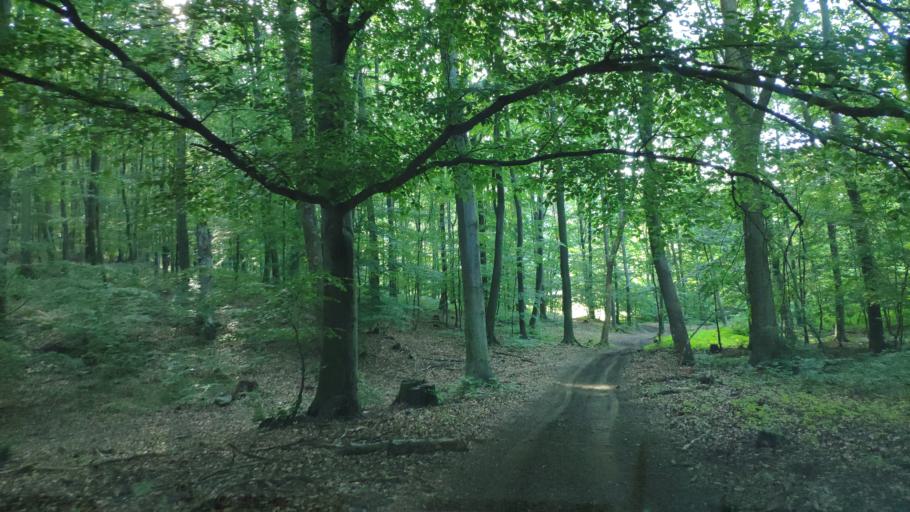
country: SK
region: Presovsky
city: Vranov nad Topl'ou
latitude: 48.8147
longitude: 21.5930
